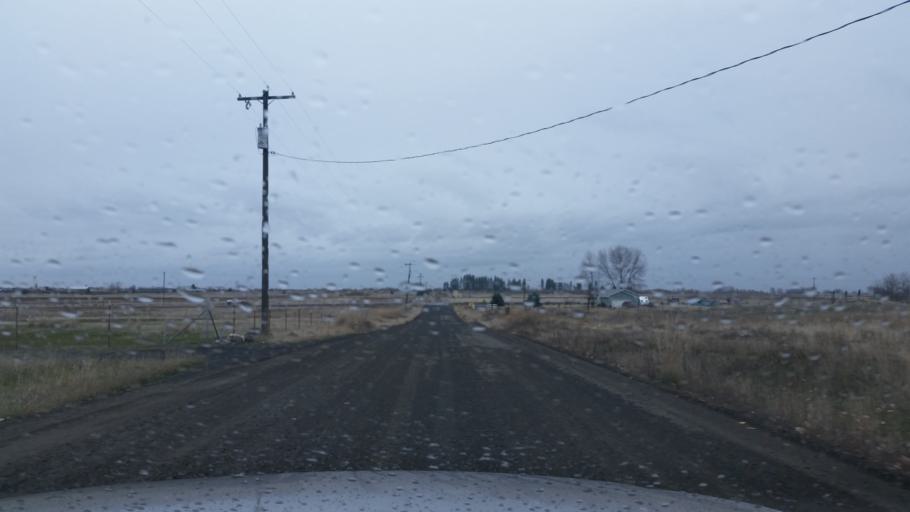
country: US
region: Washington
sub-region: Spokane County
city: Fairchild Air Force Base
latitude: 47.5885
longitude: -117.6289
